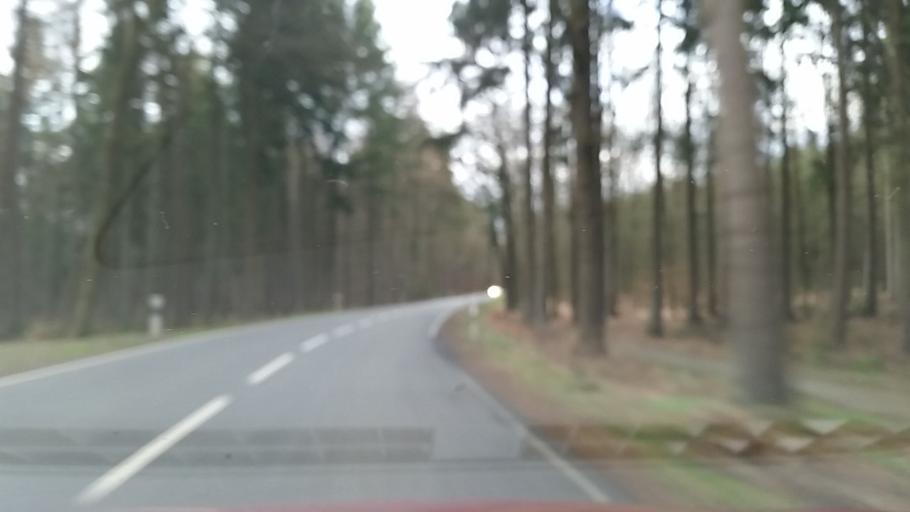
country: DE
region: Lower Saxony
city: Zernien
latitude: 53.1054
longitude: 10.9443
